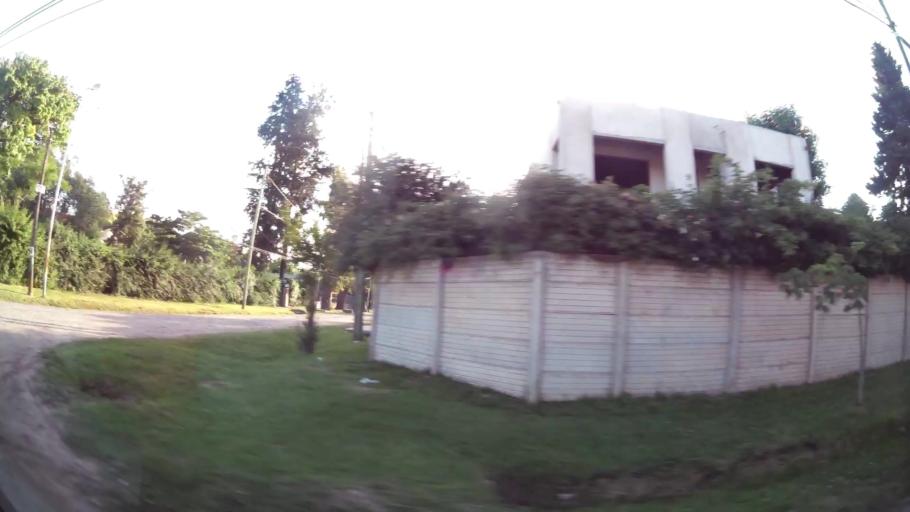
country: AR
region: Buenos Aires
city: Santa Catalina - Dique Lujan
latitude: -34.4660
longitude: -58.7463
